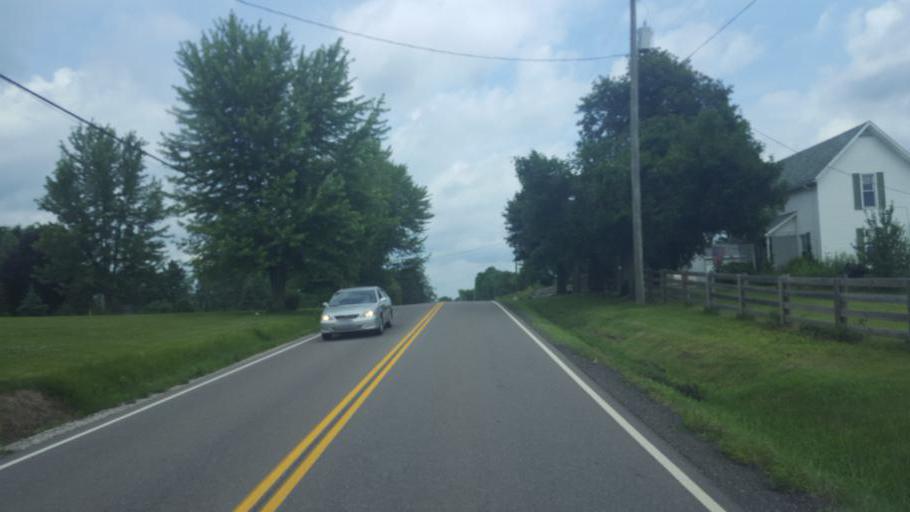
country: US
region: Ohio
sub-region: Knox County
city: Mount Vernon
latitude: 40.3269
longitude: -82.5076
